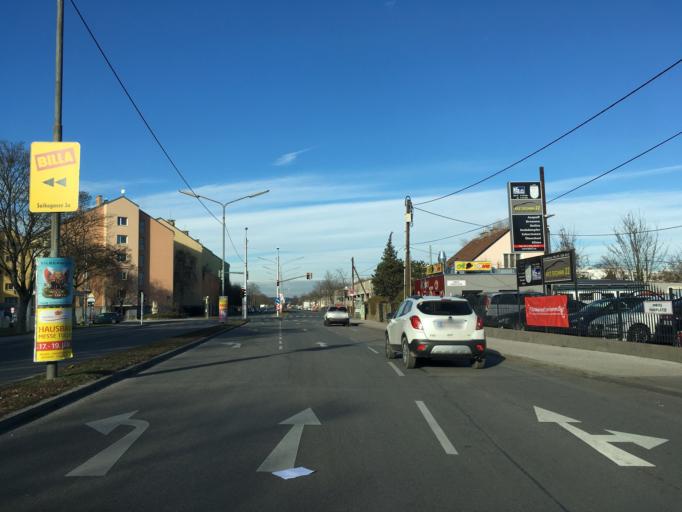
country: AT
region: Lower Austria
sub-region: Politischer Bezirk Wien-Umgebung
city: Gerasdorf bei Wien
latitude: 48.2556
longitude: 16.4409
